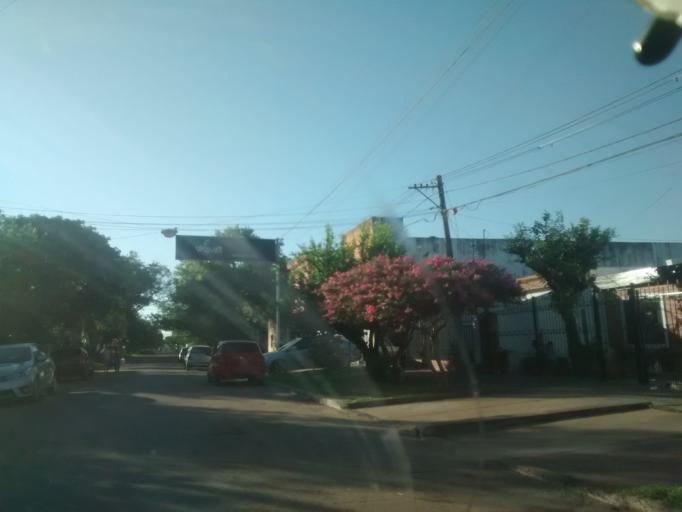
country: AR
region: Chaco
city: Resistencia
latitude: -27.4442
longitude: -59.0049
